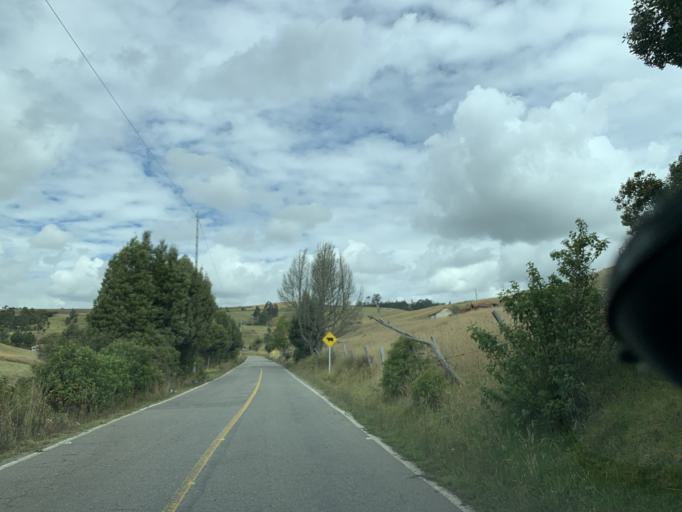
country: CO
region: Boyaca
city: Toca
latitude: 5.5719
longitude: -73.2324
